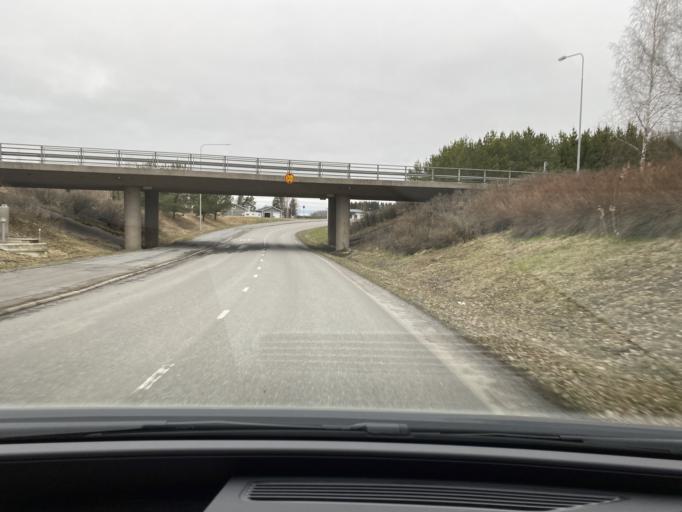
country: FI
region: Satakunta
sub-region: Pori
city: Huittinen
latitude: 61.1825
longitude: 22.6846
